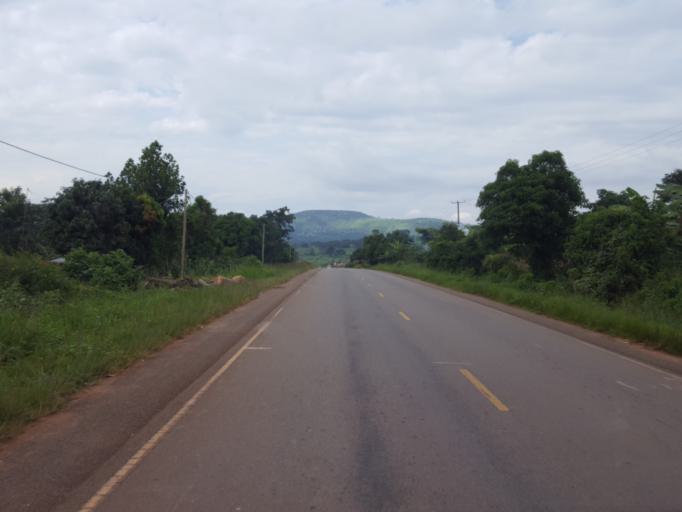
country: UG
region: Central Region
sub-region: Mityana District
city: Mityana
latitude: 0.6208
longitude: 32.1354
